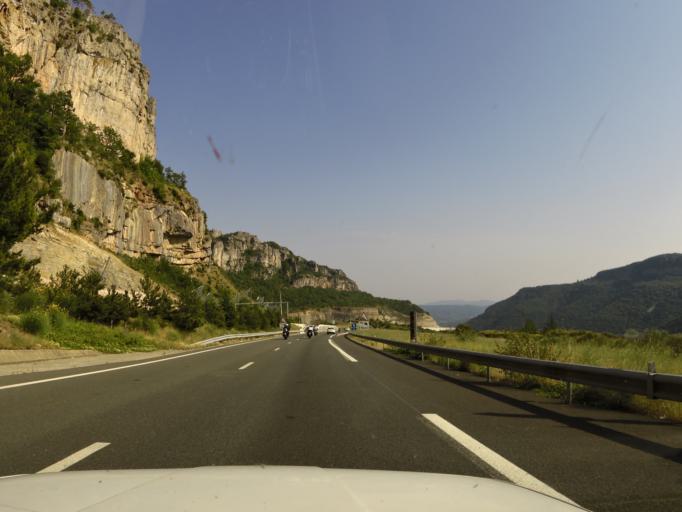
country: FR
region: Languedoc-Roussillon
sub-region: Departement de l'Herault
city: Lodeve
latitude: 43.8288
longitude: 3.3155
